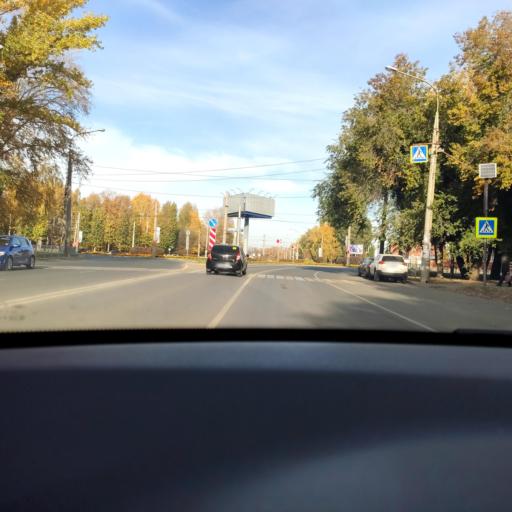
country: RU
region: Samara
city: Samara
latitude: 53.2281
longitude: 50.2081
